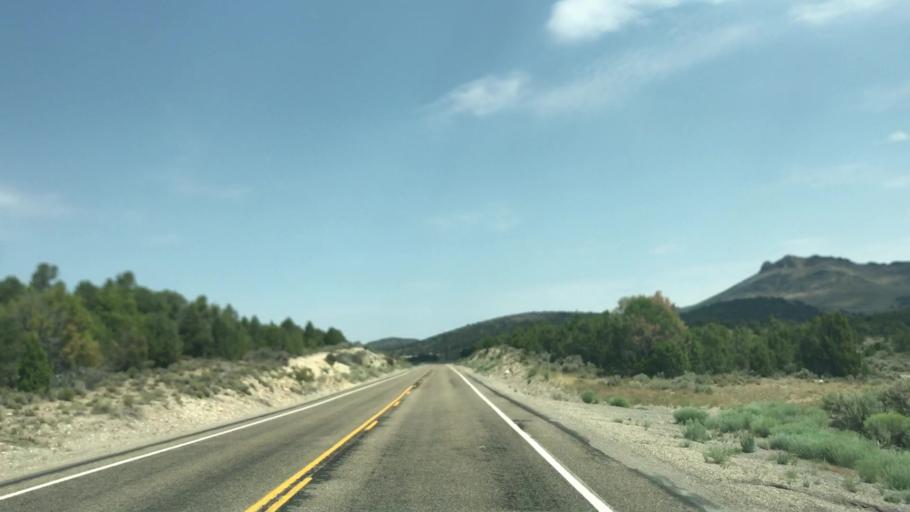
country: US
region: Nevada
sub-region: White Pine County
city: Ely
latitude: 39.3975
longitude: -115.0833
